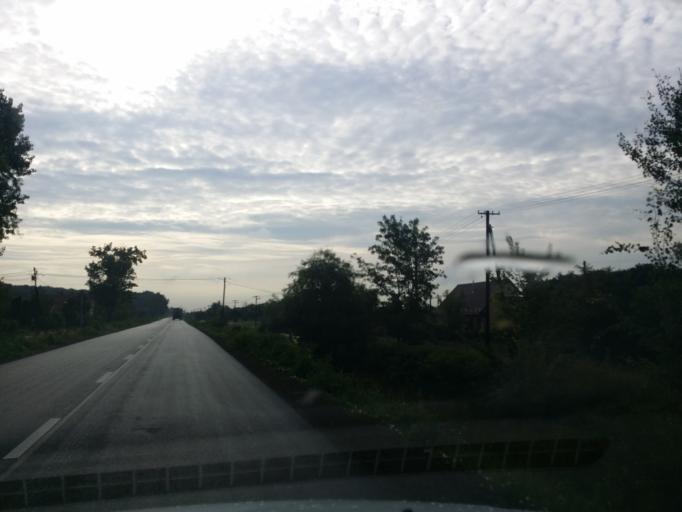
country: HU
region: Heves
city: Poroszlo
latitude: 47.6261
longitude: 20.5986
